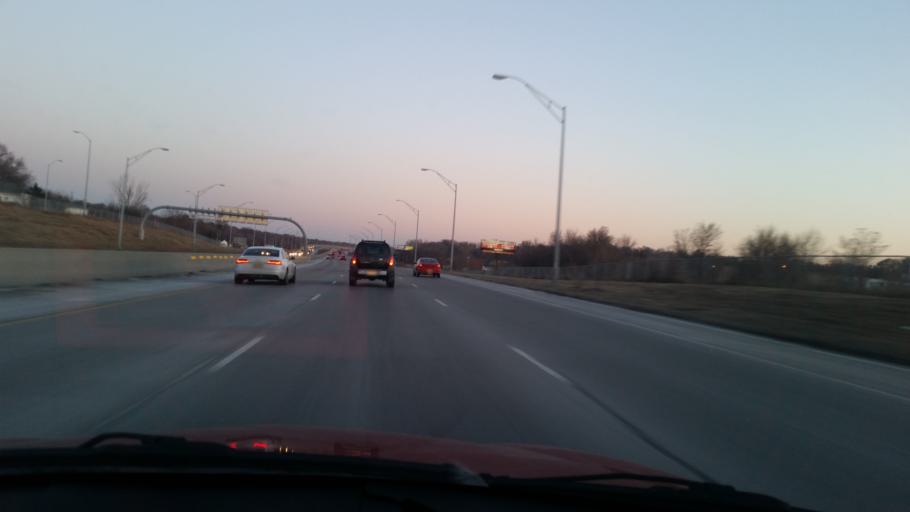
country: US
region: Nebraska
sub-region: Douglas County
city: Omaha
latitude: 41.2012
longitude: -95.9474
